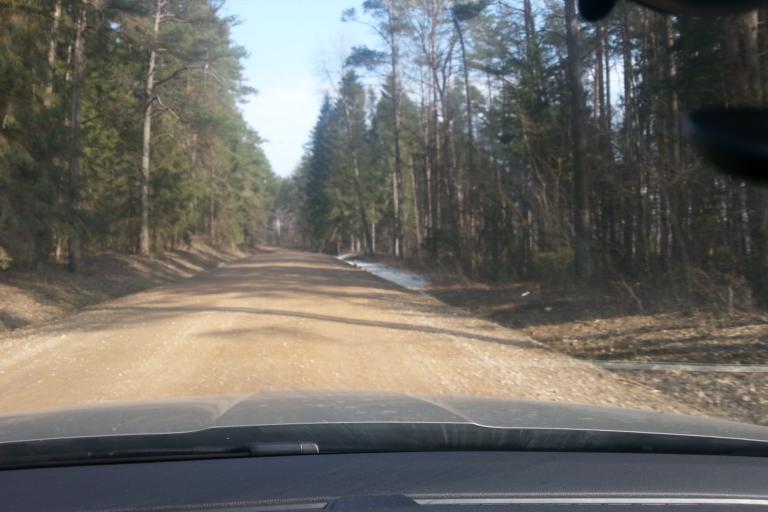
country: LT
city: Trakai
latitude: 54.5776
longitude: 24.9707
